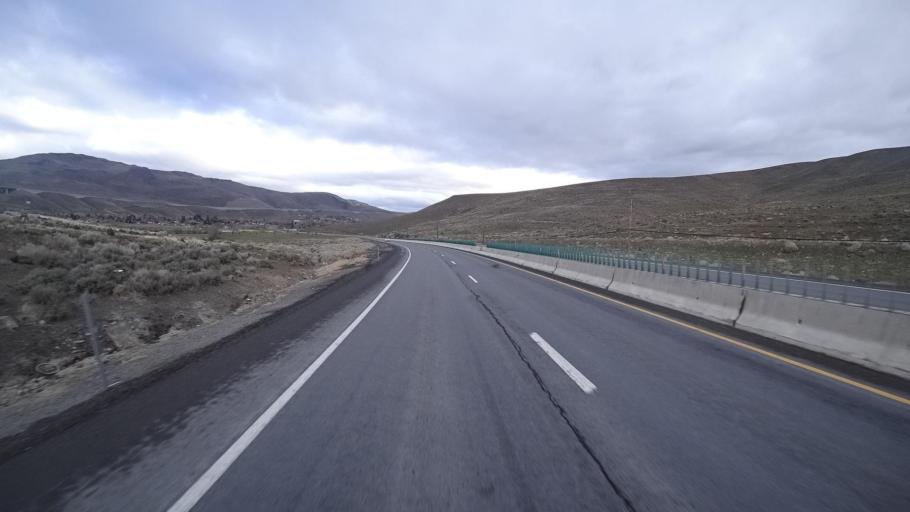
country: US
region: Nevada
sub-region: Storey County
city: Virginia City
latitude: 39.3368
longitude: -119.7796
